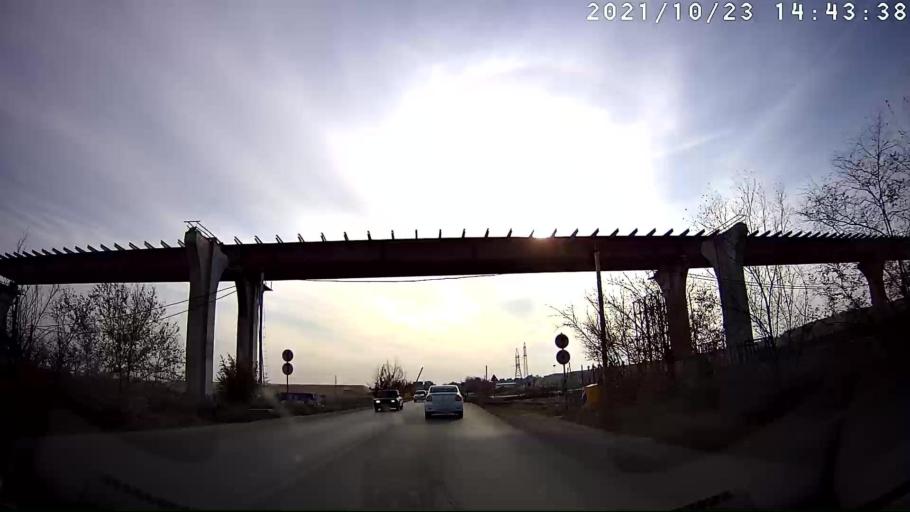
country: RU
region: Volgograd
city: Krasnoslobodsk
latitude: 48.4588
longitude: 44.5230
